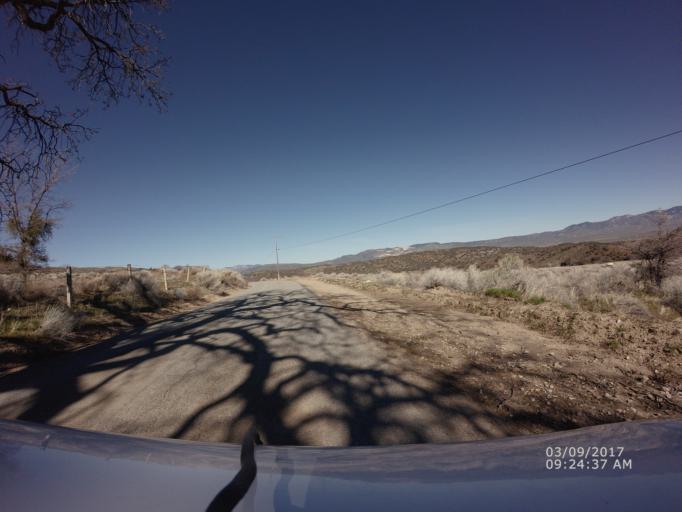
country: US
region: California
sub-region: Kern County
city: Lebec
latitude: 34.7486
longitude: -118.6823
